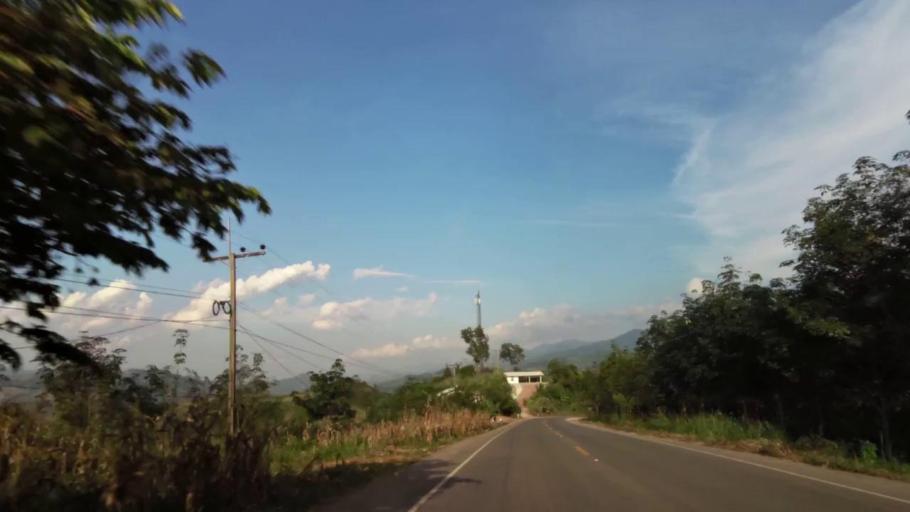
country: TH
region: Chiang Rai
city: Khun Tan
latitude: 19.8580
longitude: 100.3891
